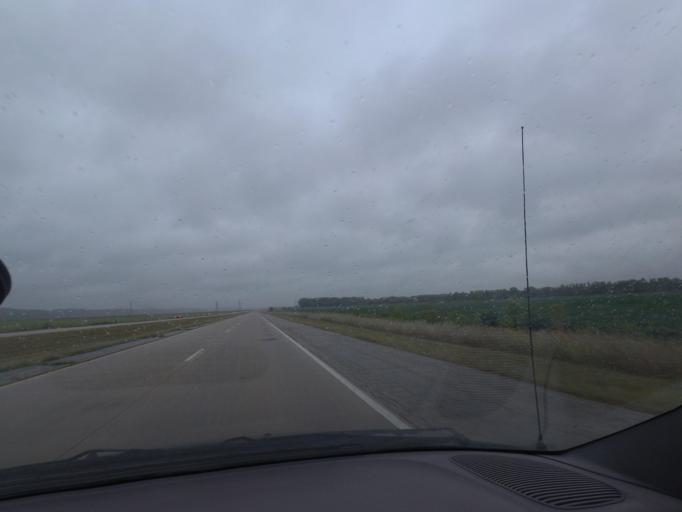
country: US
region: Illinois
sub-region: Adams County
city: Payson
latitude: 39.7367
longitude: -91.2487
